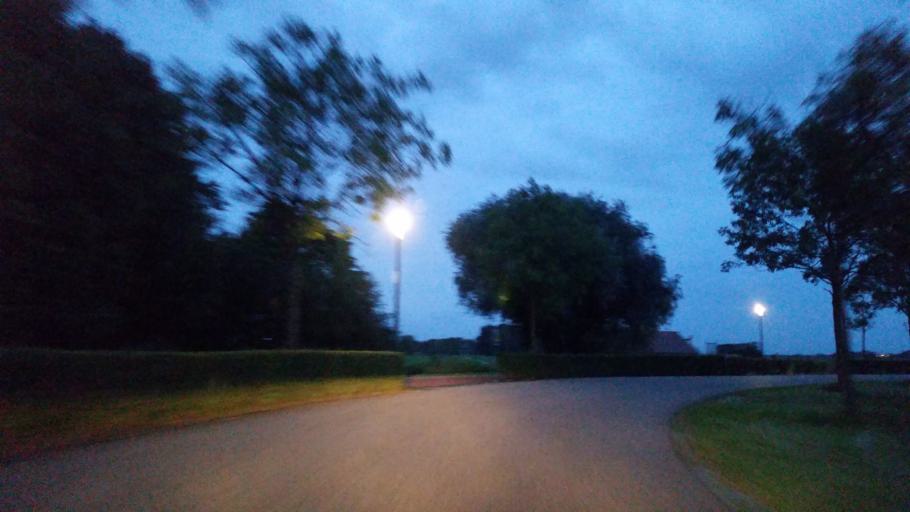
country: NL
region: Friesland
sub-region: Gemeente Leeuwarden
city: Camminghaburen
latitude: 53.2271
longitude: 5.8217
